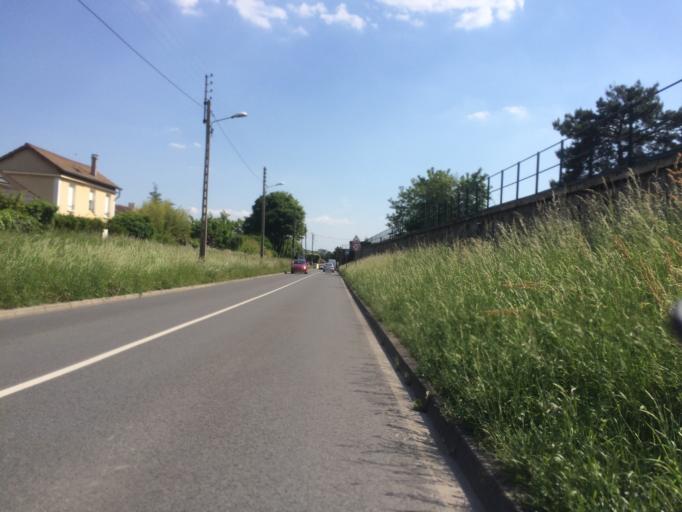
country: FR
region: Ile-de-France
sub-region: Departement de l'Essonne
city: Savigny-sur-Orge
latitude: 48.6849
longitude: 2.3595
